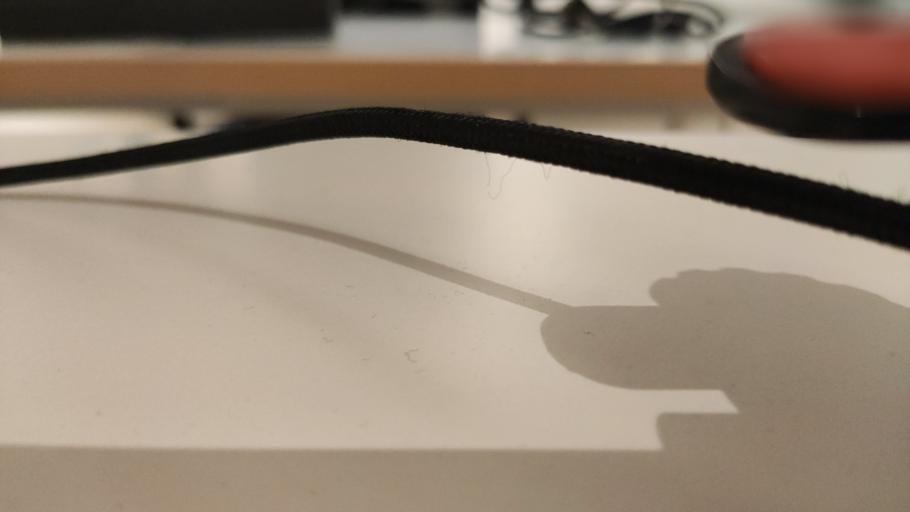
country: RU
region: Moskovskaya
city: Dorokhovo
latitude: 55.4788
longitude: 36.3573
